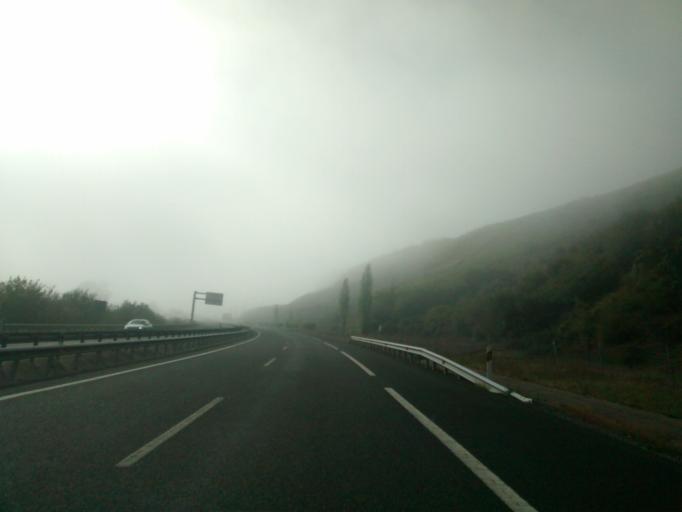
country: ES
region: Cantabria
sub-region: Provincia de Cantabria
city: Arenas de Iguna
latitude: 43.1783
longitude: -4.0567
